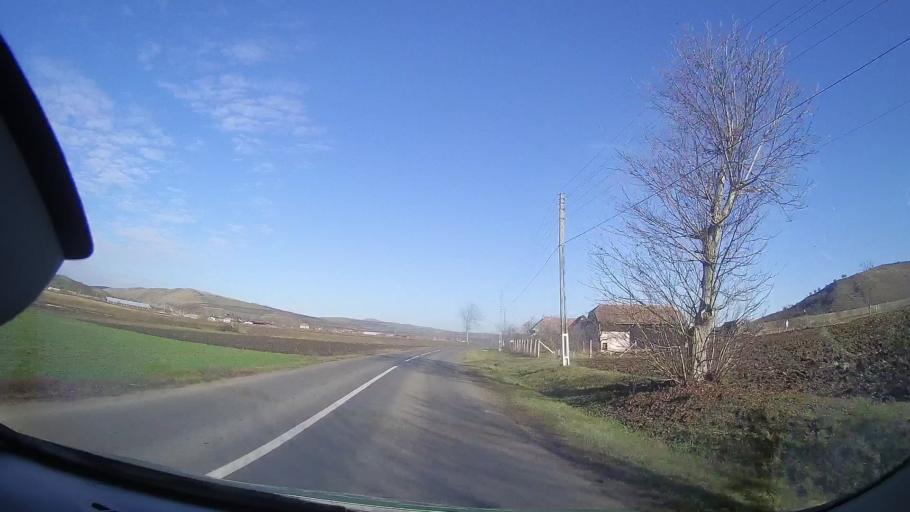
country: RO
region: Mures
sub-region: Comuna Grebenisu de Campie
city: Grebenisu de Campie
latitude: 46.5604
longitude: 24.3344
